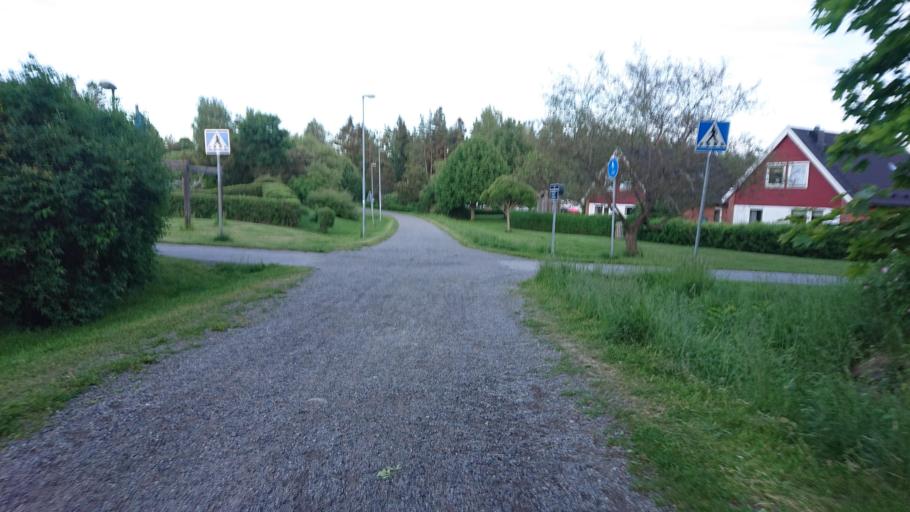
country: SE
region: Stockholm
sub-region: Osterakers Kommun
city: Akersberga
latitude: 59.5036
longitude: 18.3047
